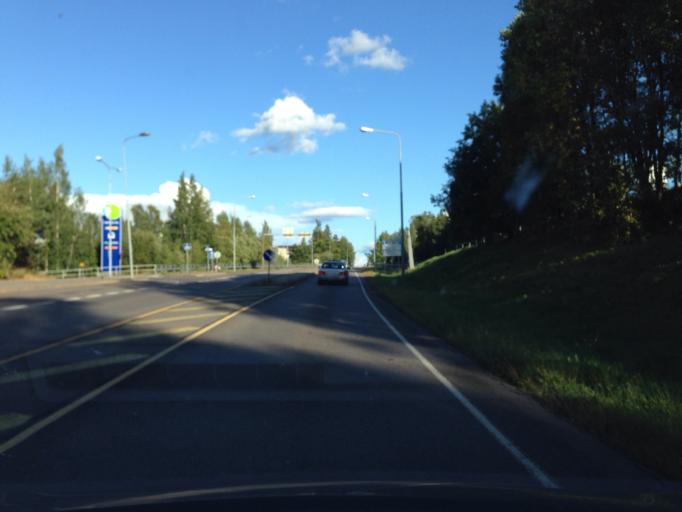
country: FI
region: Uusimaa
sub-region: Helsinki
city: Kerava
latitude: 60.3466
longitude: 25.0807
